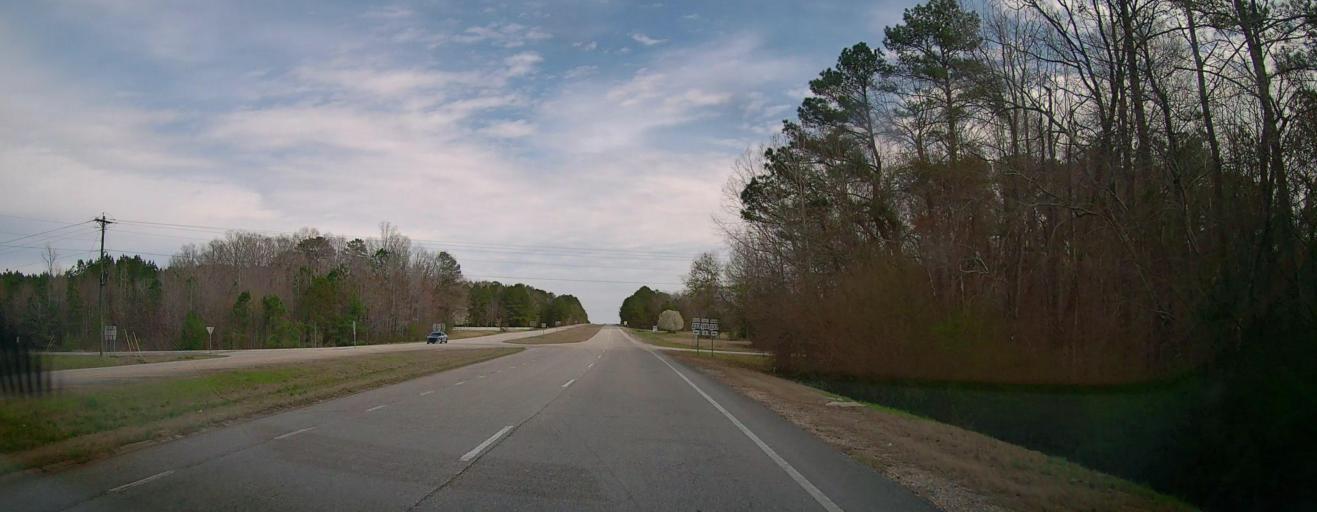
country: US
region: Alabama
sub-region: Marion County
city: Winfield
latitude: 33.9333
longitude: -87.7076
